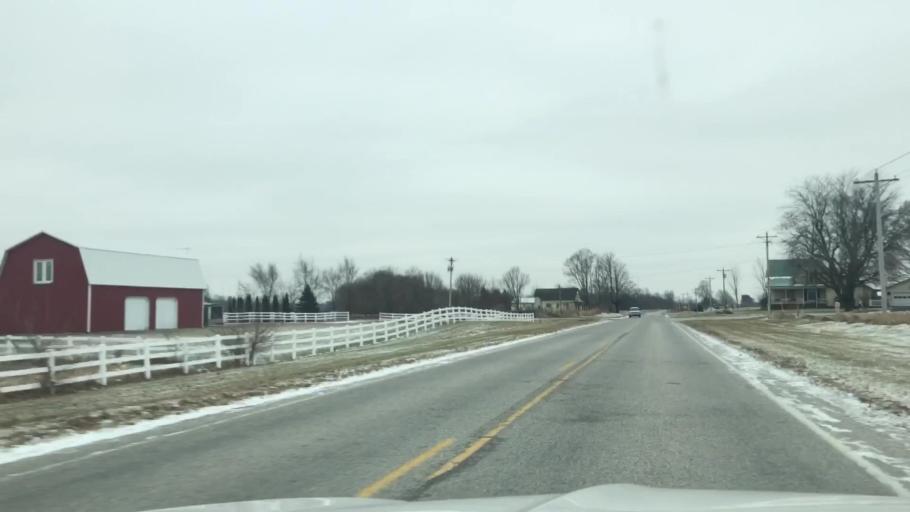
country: US
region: Indiana
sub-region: Fulton County
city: Rochester
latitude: 41.0335
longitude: -86.1986
